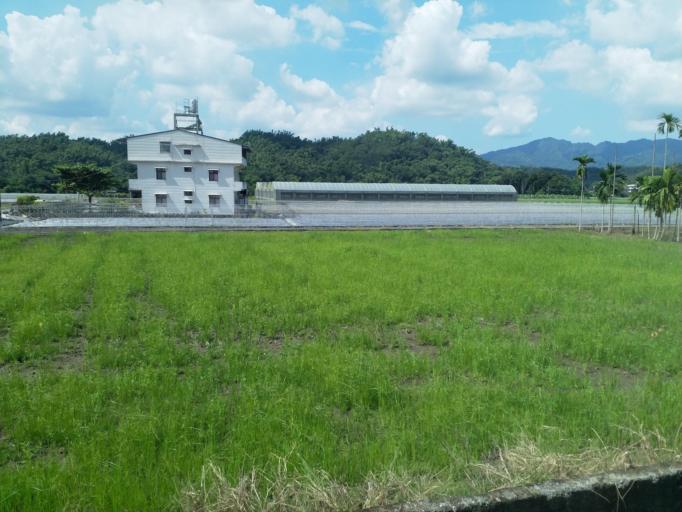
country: TW
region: Taiwan
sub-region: Pingtung
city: Pingtung
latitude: 22.8858
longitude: 120.5786
